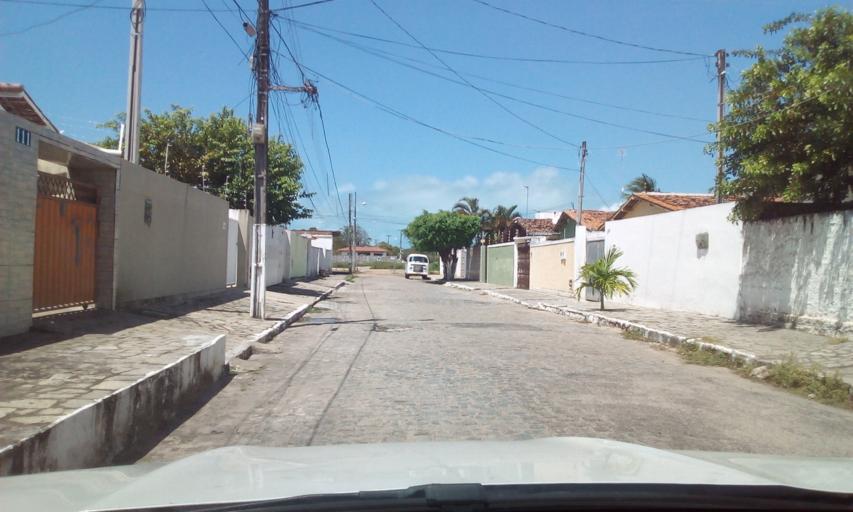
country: BR
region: Paraiba
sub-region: Joao Pessoa
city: Joao Pessoa
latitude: -7.1677
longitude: -34.8296
